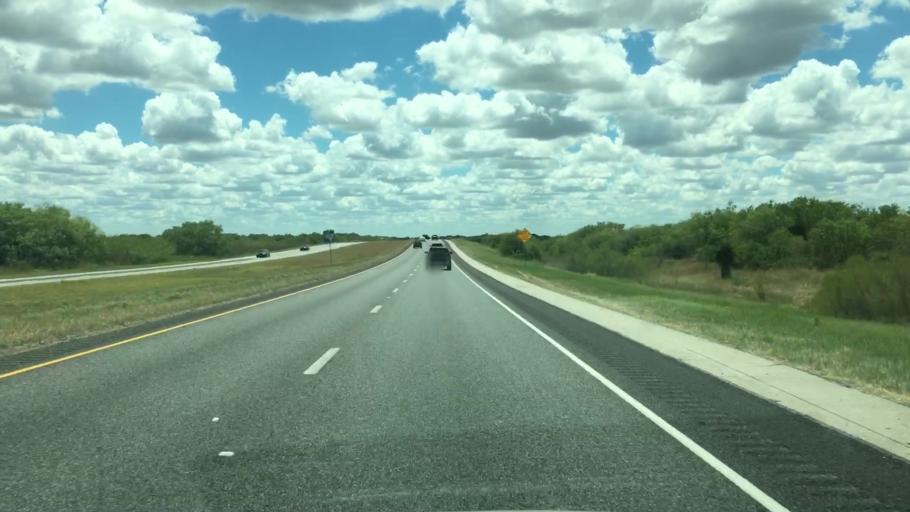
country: US
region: Texas
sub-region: Atascosa County
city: Pleasanton
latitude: 29.0908
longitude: -98.4331
